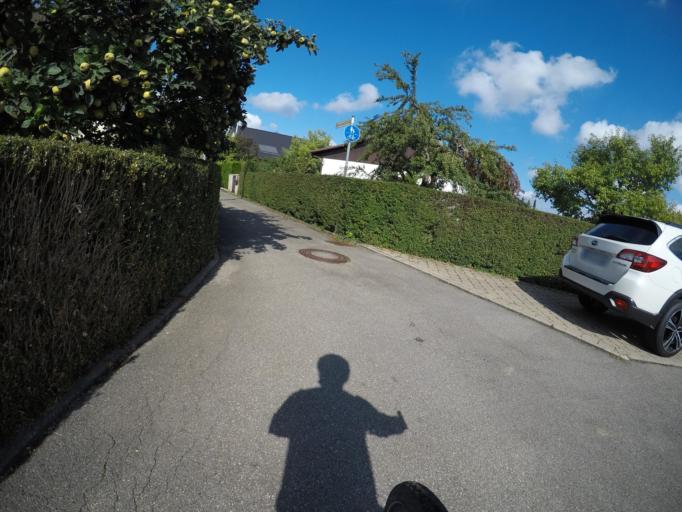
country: DE
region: Baden-Wuerttemberg
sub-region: Regierungsbezirk Stuttgart
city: Herrenberg
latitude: 48.6135
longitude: 8.8445
